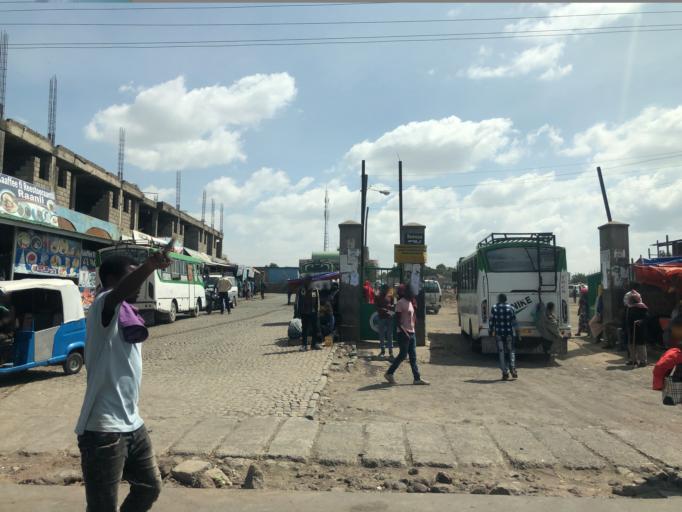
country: ET
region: Oromiya
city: Shashemene
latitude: 7.2047
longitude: 38.6098
